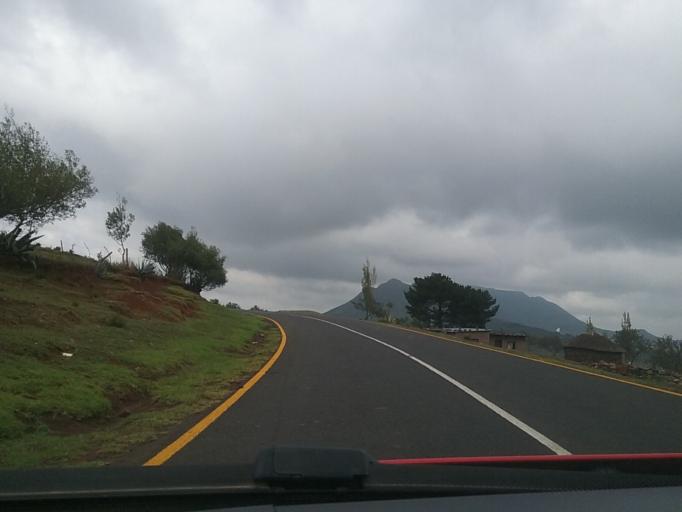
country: LS
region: Berea
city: Teyateyaneng
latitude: -29.2354
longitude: 27.8630
